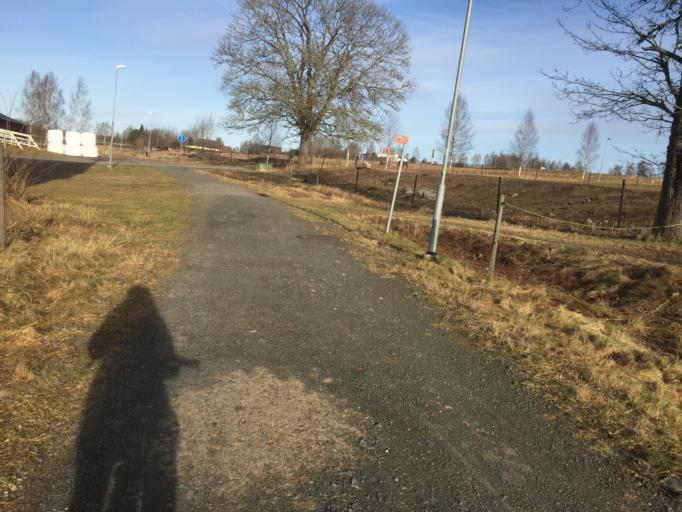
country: SE
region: Joenkoeping
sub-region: Aneby Kommun
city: Aneby
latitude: 57.8258
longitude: 14.8156
